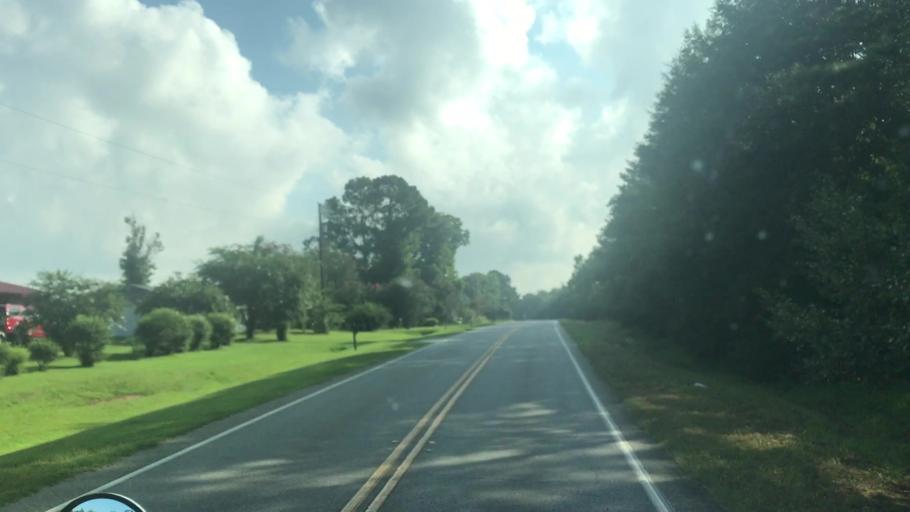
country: US
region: Florida
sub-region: Gadsden County
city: Havana
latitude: 30.7332
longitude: -84.4841
